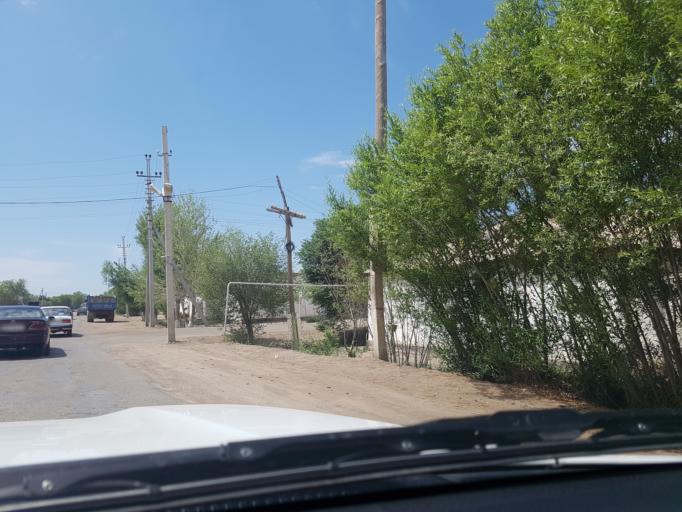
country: TM
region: Dasoguz
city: Koeneuergench
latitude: 42.3160
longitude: 59.1392
